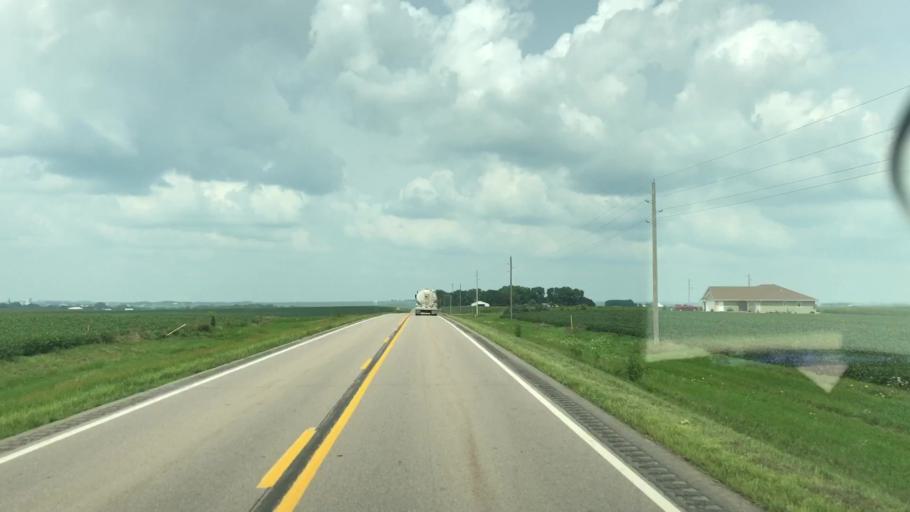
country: US
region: Iowa
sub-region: Plymouth County
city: Remsen
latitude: 42.7915
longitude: -95.9578
